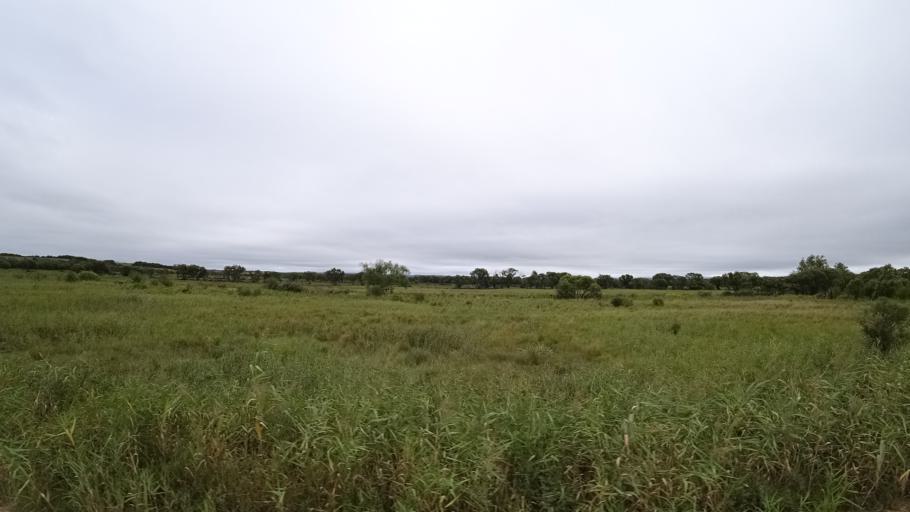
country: RU
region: Primorskiy
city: Ivanovka
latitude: 44.0713
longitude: 132.5808
